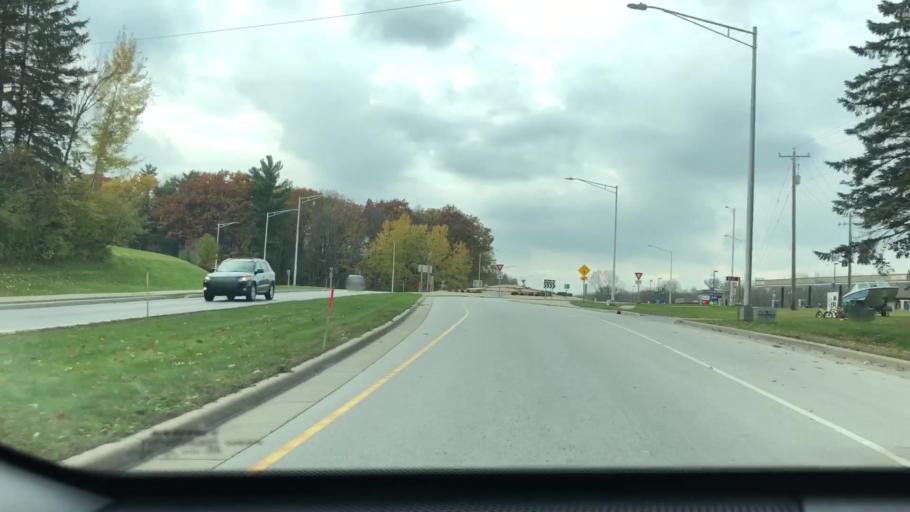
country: US
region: Wisconsin
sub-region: Brown County
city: Oneida
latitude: 44.5009
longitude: -88.1923
